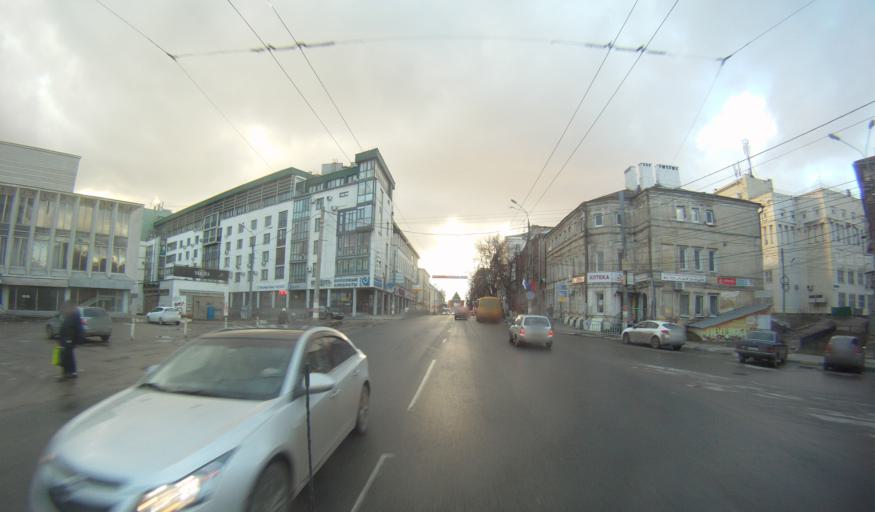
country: RU
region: Nizjnij Novgorod
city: Nizhniy Novgorod
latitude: 56.3232
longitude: 44.0104
